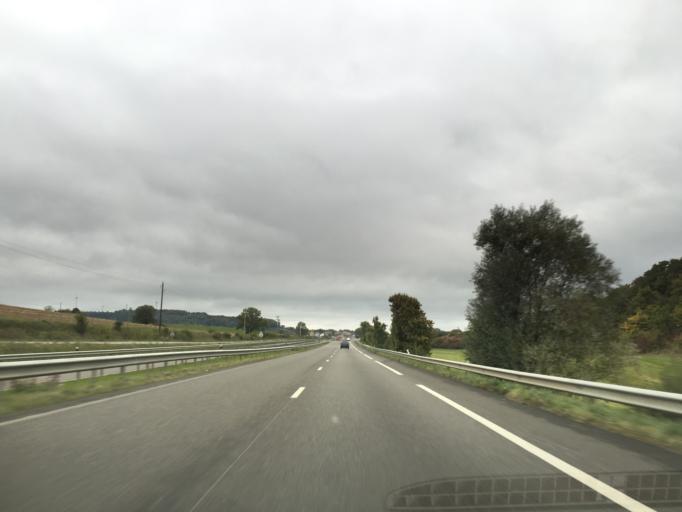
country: FR
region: Lorraine
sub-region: Departement de la Meuse
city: Vacon
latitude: 48.6959
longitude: 5.5454
